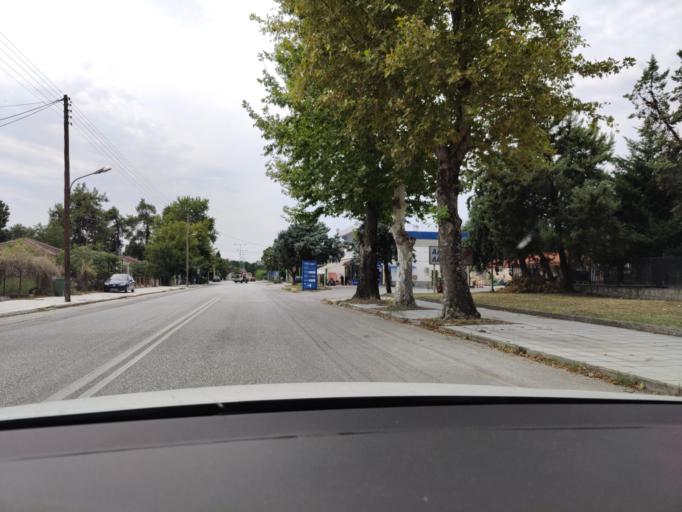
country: GR
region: Central Macedonia
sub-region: Nomos Serron
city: Serres
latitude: 41.0776
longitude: 23.5391
